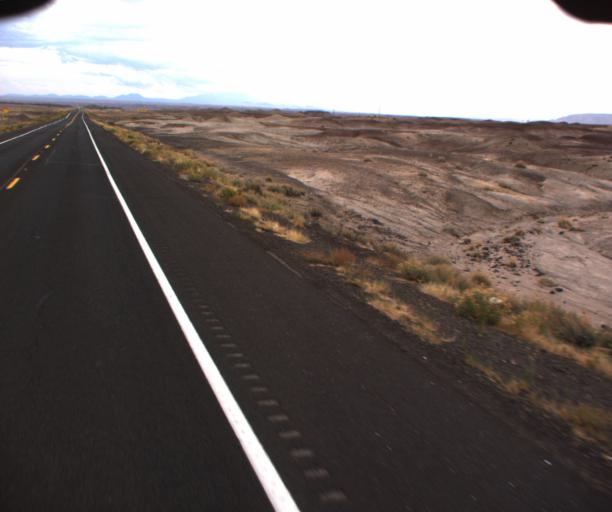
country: US
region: Arizona
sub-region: Coconino County
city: Tuba City
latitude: 35.9613
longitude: -111.3971
